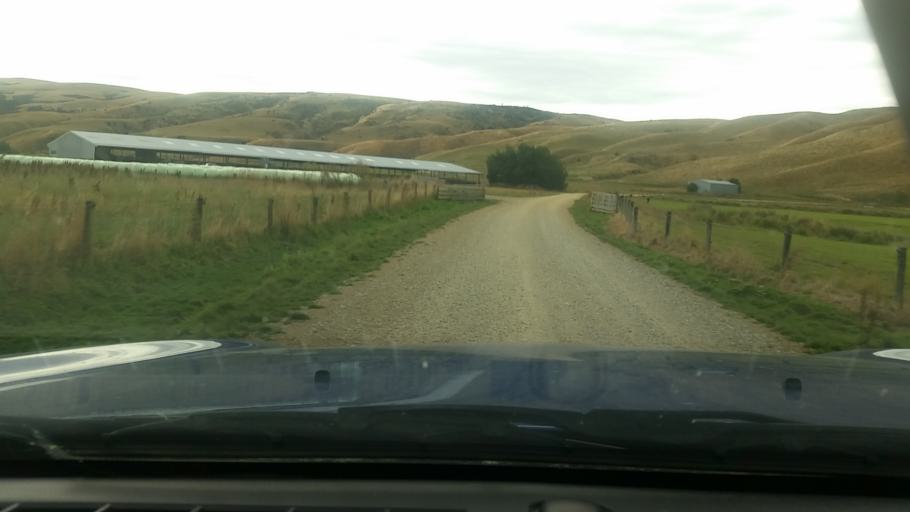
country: NZ
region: Otago
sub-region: Clutha District
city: Balclutha
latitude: -45.7227
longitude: 169.5394
